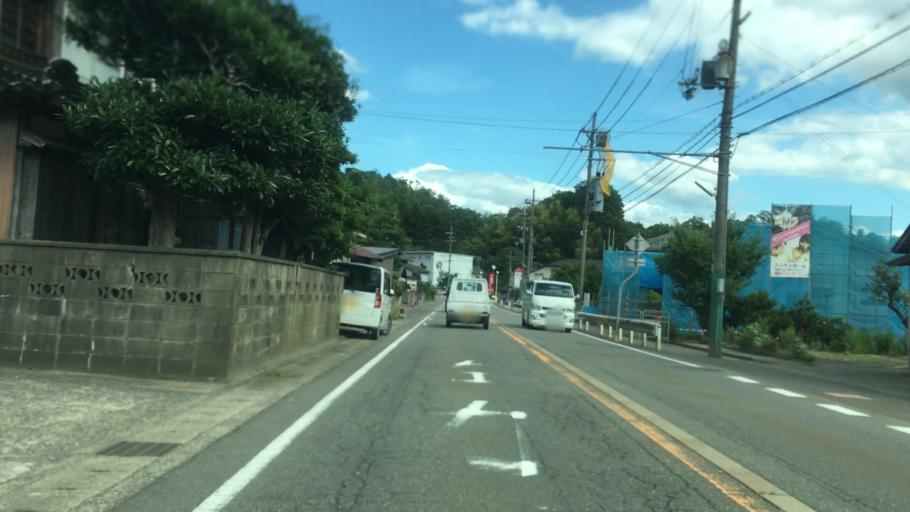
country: JP
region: Hyogo
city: Toyooka
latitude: 35.5544
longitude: 134.7989
